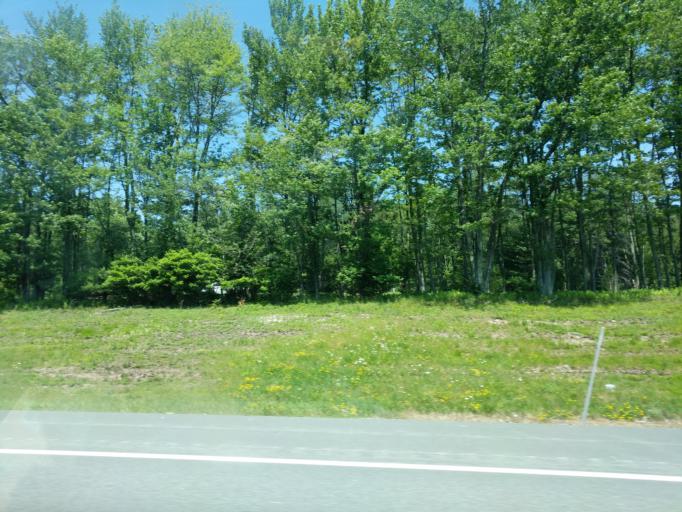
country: US
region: New York
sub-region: Sullivan County
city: Monticello
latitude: 41.6481
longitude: -74.6541
